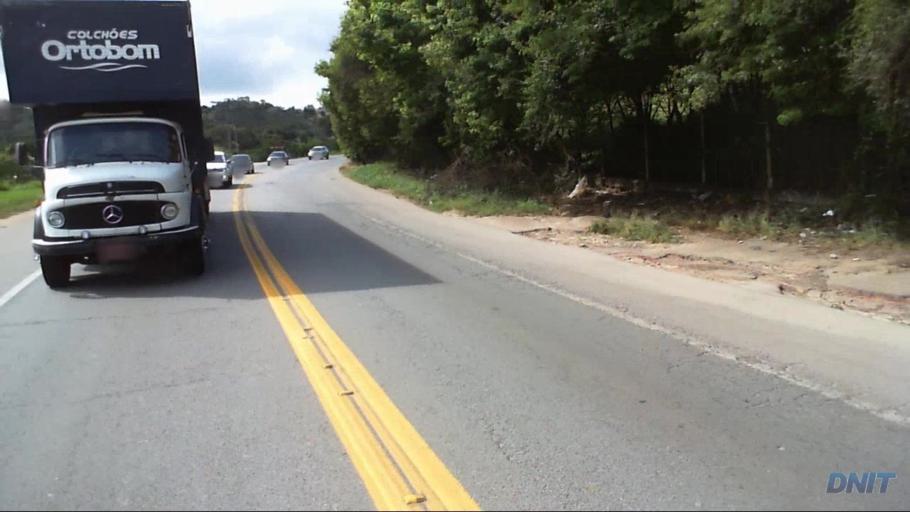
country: BR
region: Minas Gerais
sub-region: Santa Luzia
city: Santa Luzia
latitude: -19.8235
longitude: -43.8187
